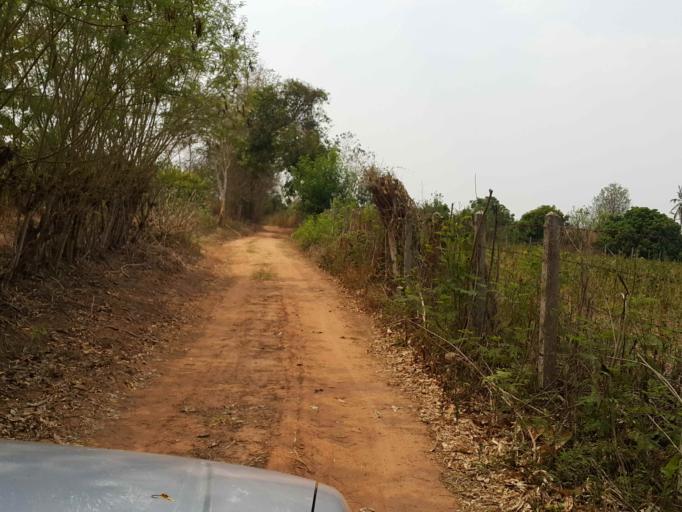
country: TH
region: Chiang Mai
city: Mae Taeng
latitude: 19.1167
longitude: 98.9963
